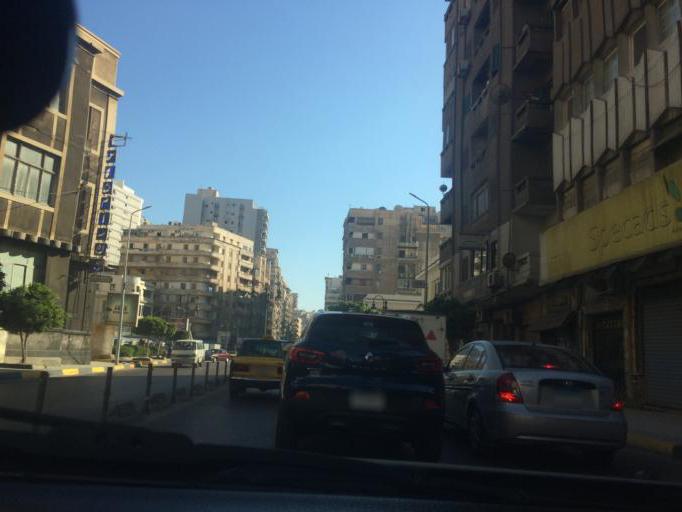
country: EG
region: Alexandria
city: Alexandria
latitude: 31.2333
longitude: 29.9577
